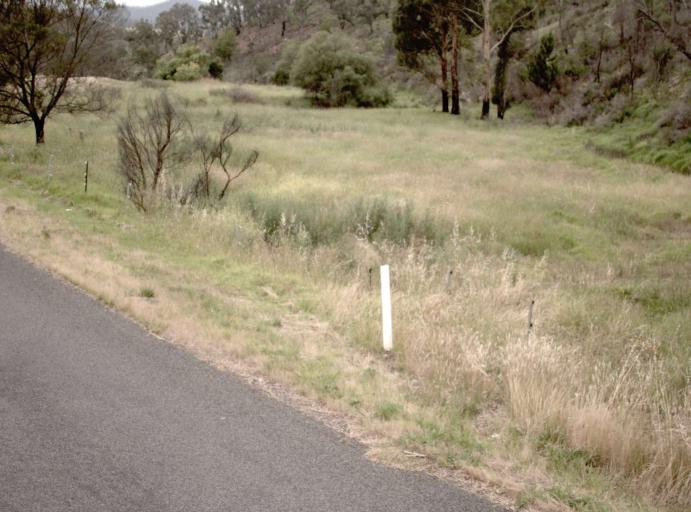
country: AU
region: Victoria
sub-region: Wellington
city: Heyfield
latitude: -37.8550
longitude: 146.7064
